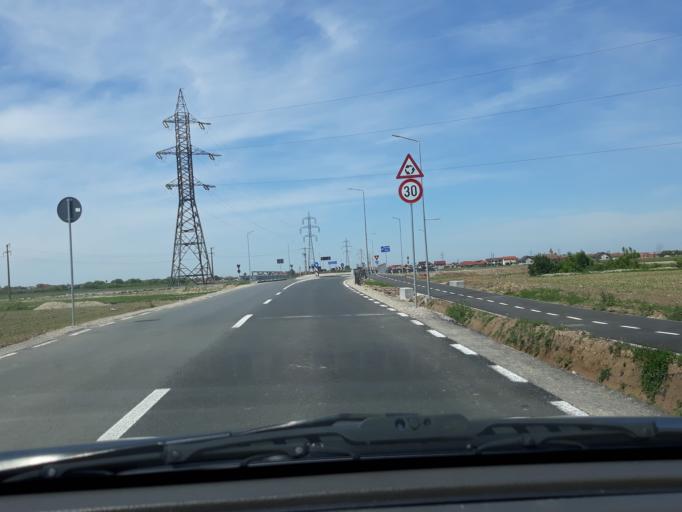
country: RO
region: Bihor
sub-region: Comuna Santandrei
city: Santandrei
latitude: 47.0668
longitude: 21.8789
